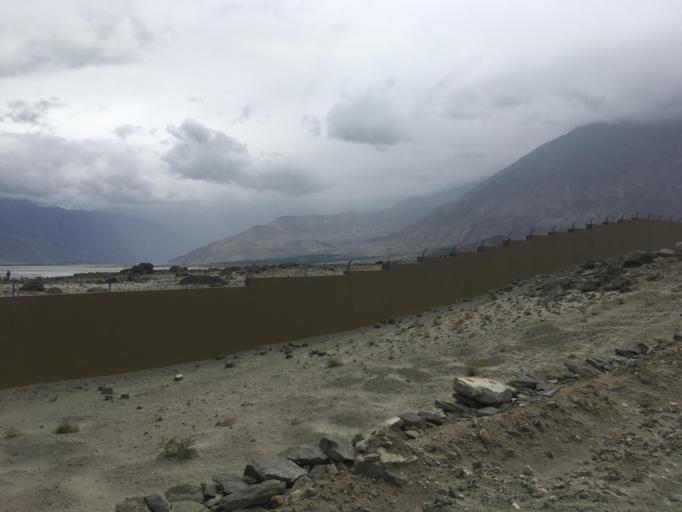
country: PK
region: Gilgit-Baltistan
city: Skardu
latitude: 35.3202
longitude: 75.6557
